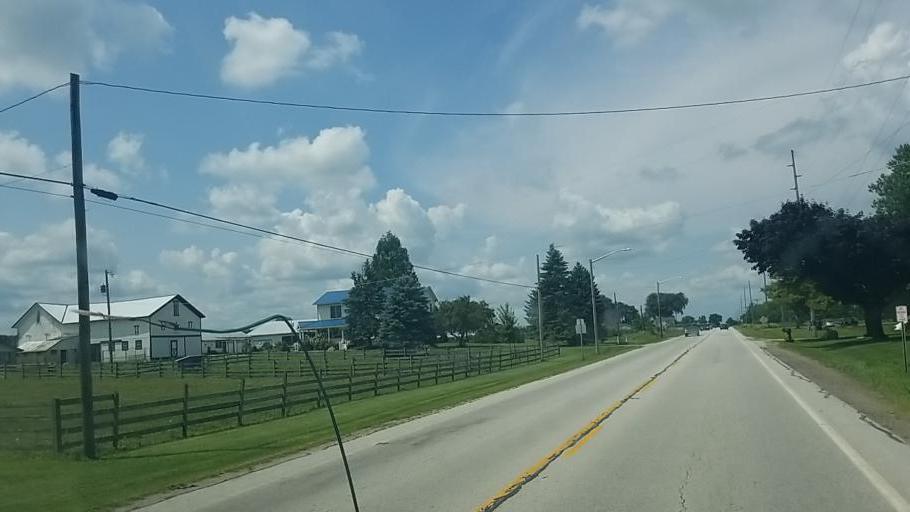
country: US
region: Ohio
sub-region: Wayne County
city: West Salem
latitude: 41.0272
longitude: -82.1277
